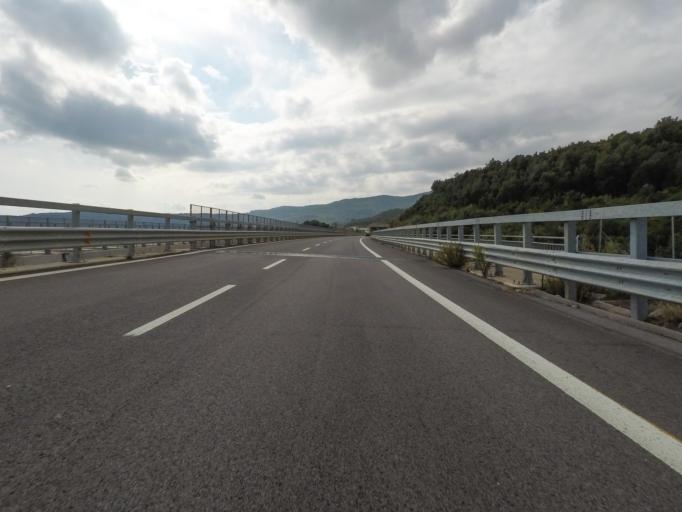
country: IT
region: Tuscany
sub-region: Provincia di Grosseto
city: Civitella Marittima
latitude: 43.0937
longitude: 11.2988
